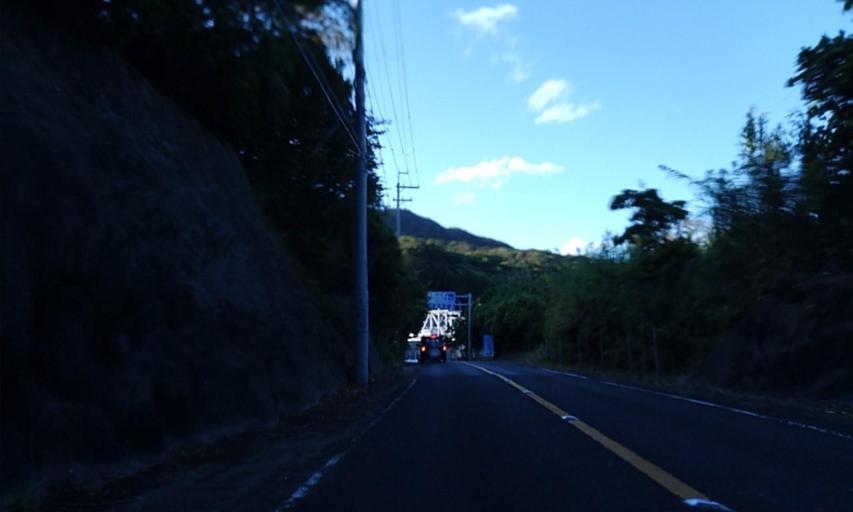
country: JP
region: Wakayama
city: Wakayama-shi
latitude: 34.3165
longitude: 135.1001
